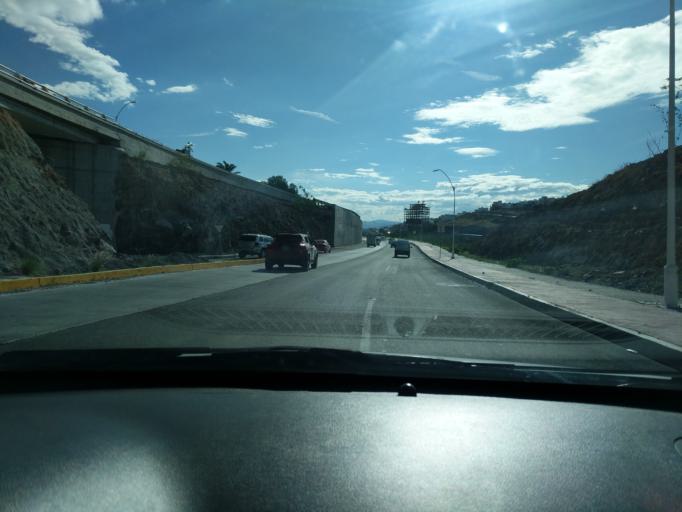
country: MX
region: Queretaro
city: La Canada
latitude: 20.5892
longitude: -100.3414
